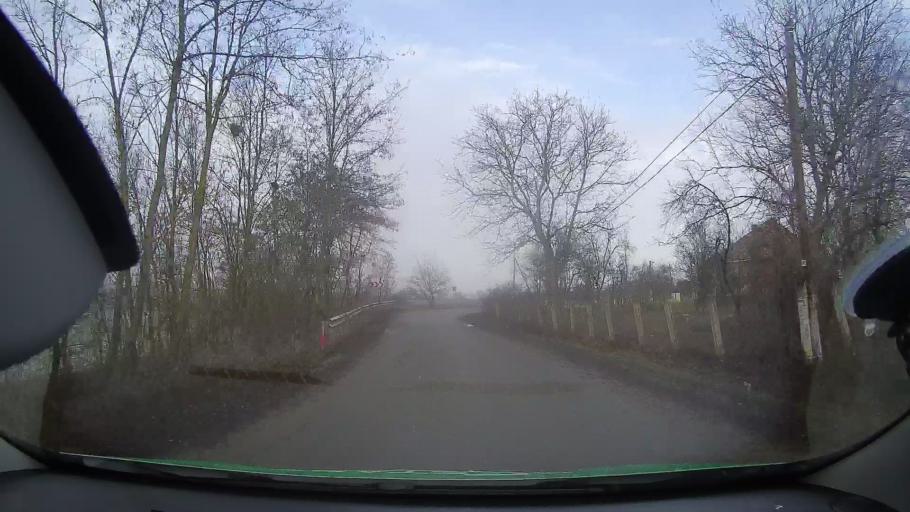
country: RO
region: Alba
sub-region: Comuna Noslac
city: Noslac
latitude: 46.4225
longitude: 23.9897
